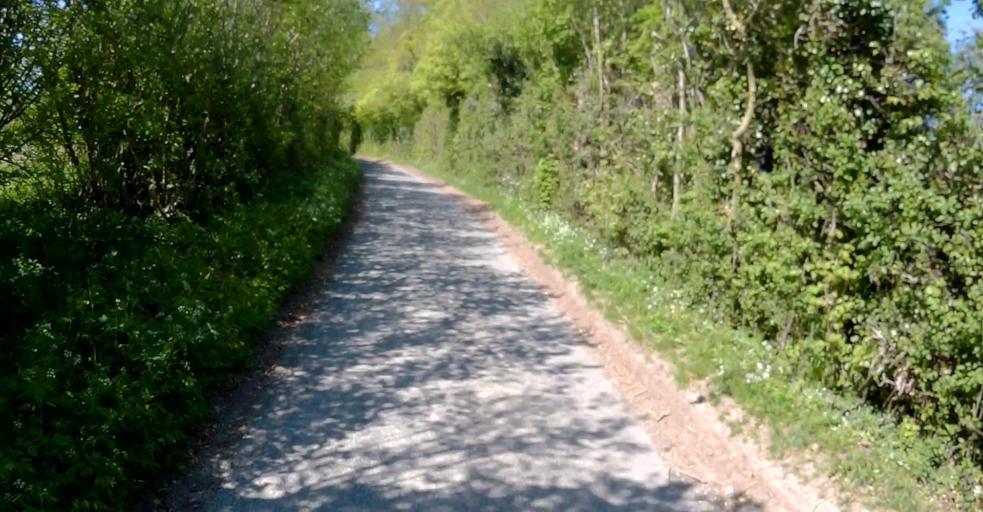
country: GB
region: England
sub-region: Hampshire
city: Overton
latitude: 51.2171
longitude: -1.3161
